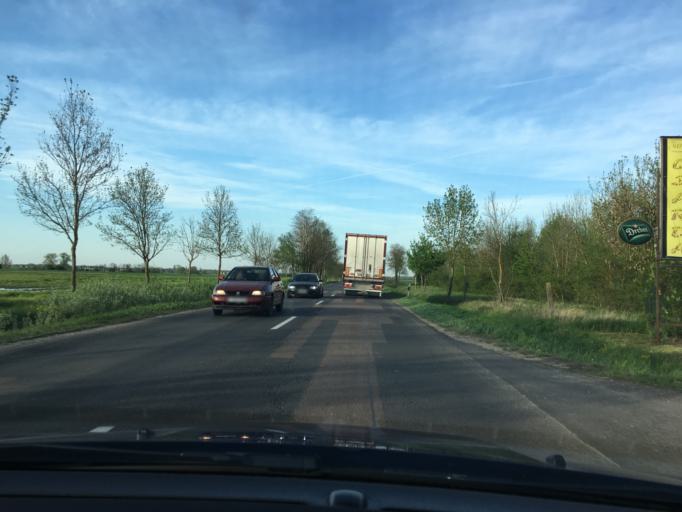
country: HU
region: Hajdu-Bihar
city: Berettyoujfalu
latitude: 47.1776
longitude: 21.5247
